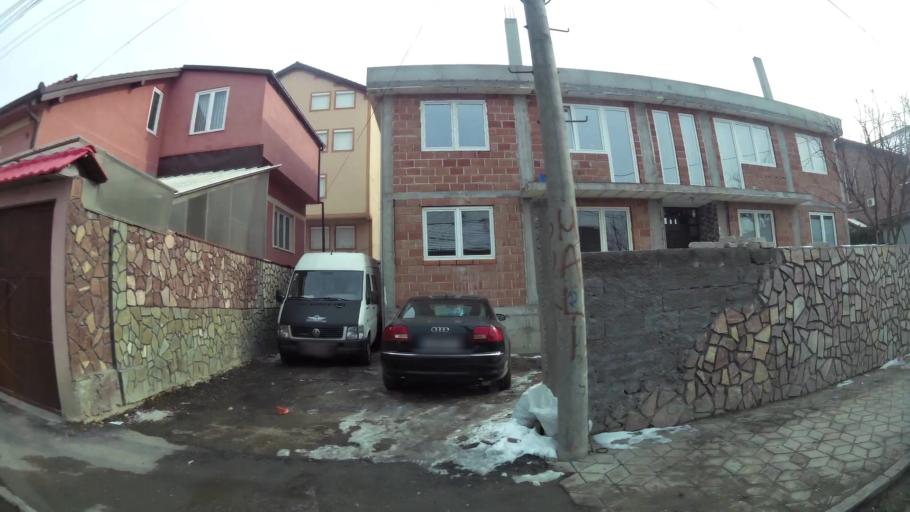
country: MK
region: Cair
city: Cair
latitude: 42.0061
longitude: 21.4471
